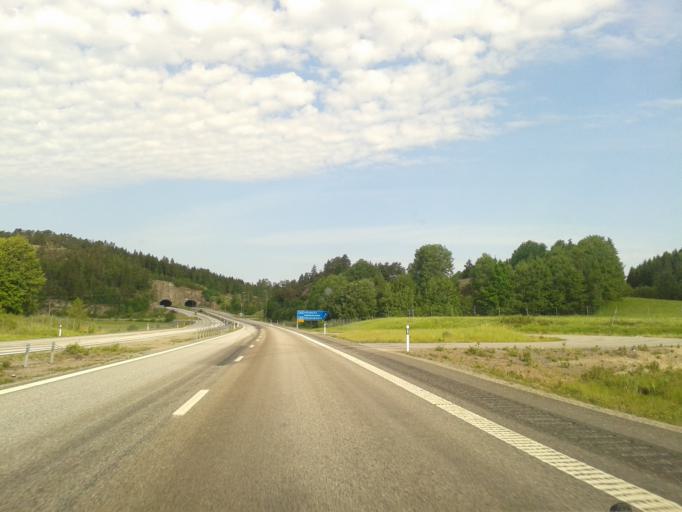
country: SE
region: Vaestra Goetaland
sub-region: Lysekils Kommun
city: Brastad
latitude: 58.5621
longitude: 11.4831
